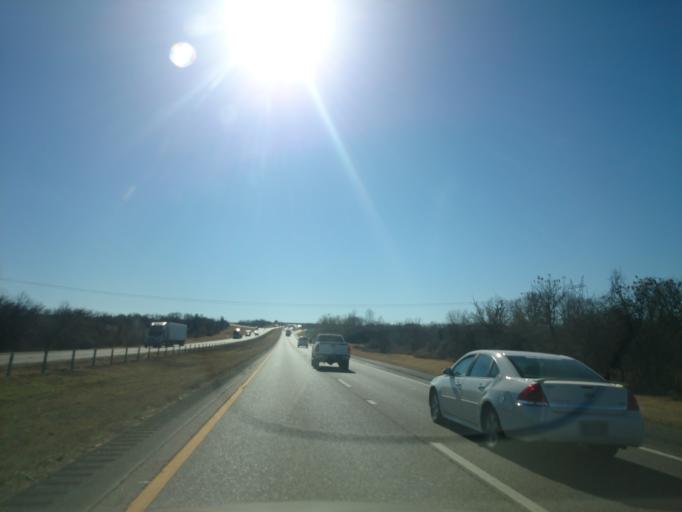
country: US
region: Oklahoma
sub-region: Oklahoma County
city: Edmond
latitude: 35.6913
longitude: -97.4163
